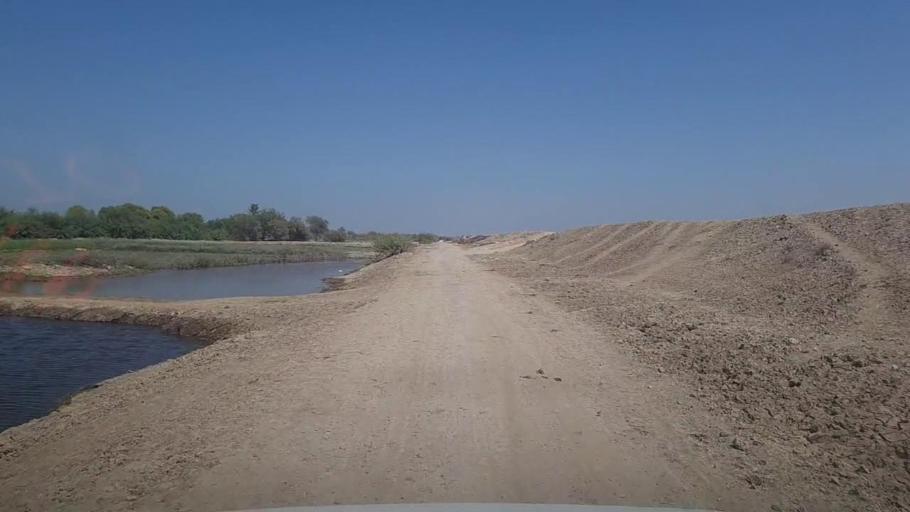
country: PK
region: Sindh
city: Kashmor
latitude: 28.2832
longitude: 69.4681
